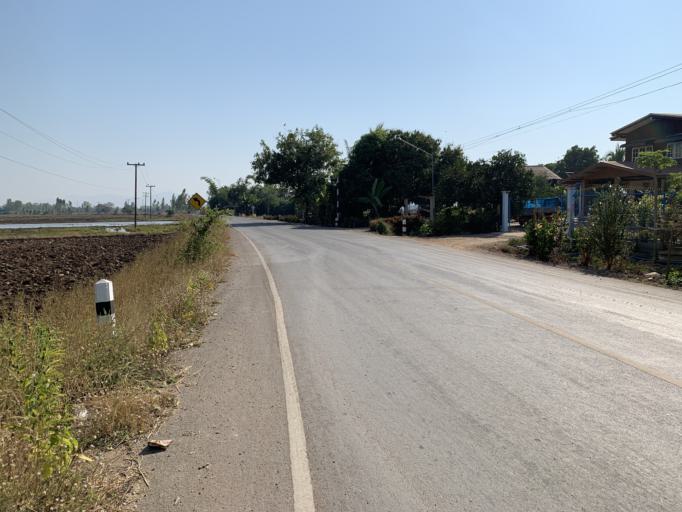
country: TH
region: Uttaradit
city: Tron
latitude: 17.3939
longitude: 100.1183
